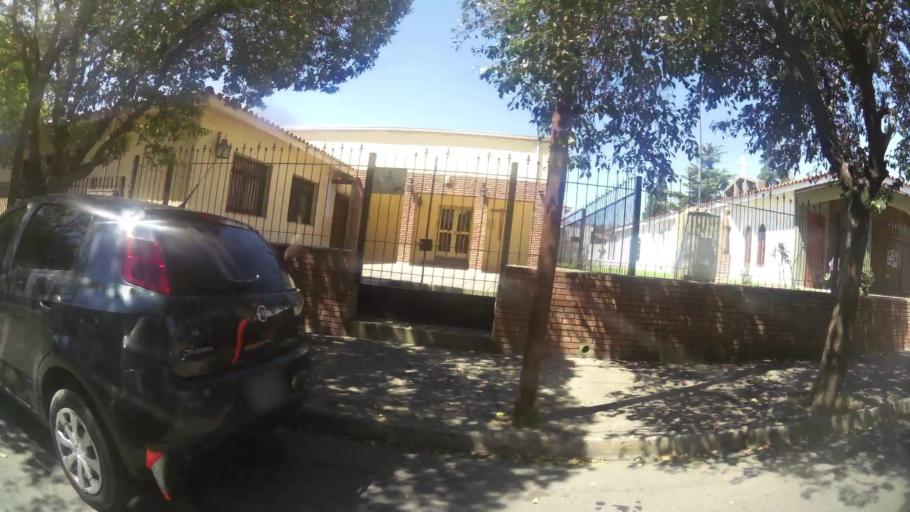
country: AR
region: Cordoba
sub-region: Departamento de Capital
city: Cordoba
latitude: -31.4196
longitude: -64.2127
